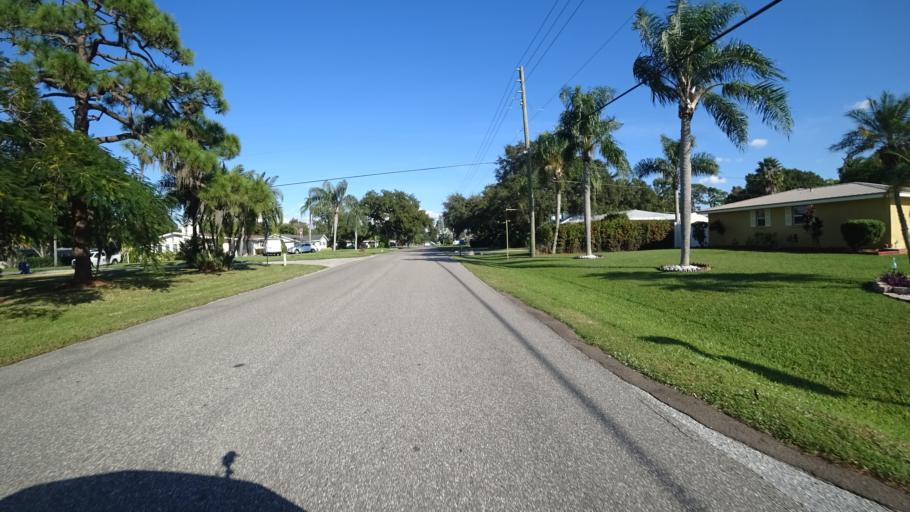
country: US
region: Florida
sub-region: Manatee County
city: West Bradenton
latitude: 27.4838
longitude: -82.6085
